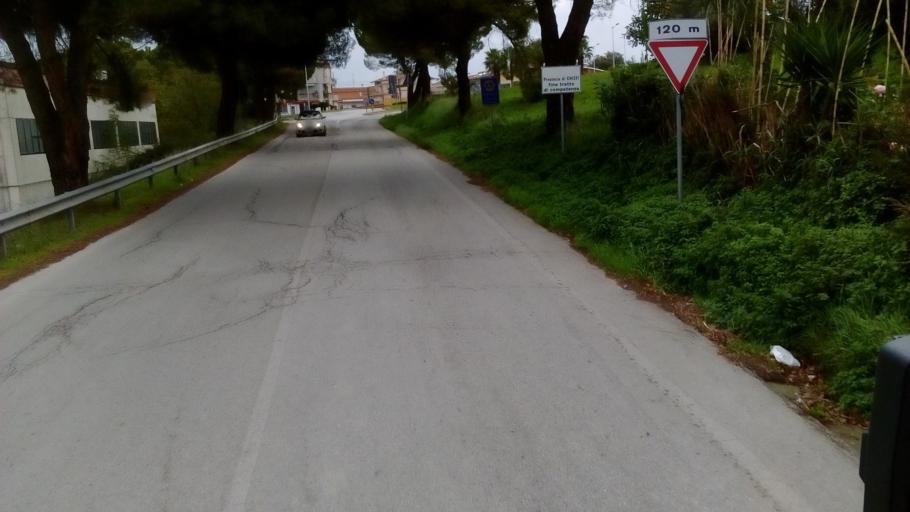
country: IT
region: Abruzzo
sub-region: Provincia di Chieti
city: San Salvo
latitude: 42.0557
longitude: 14.7324
